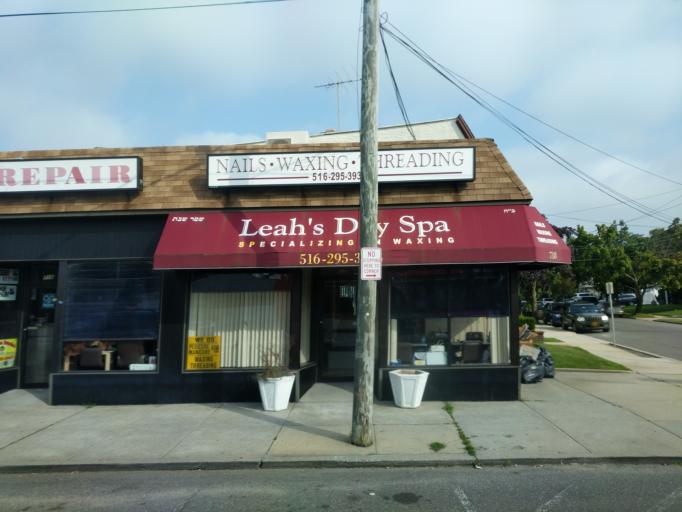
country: US
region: New York
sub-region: Nassau County
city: Cedarhurst
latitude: 40.6281
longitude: -73.7213
